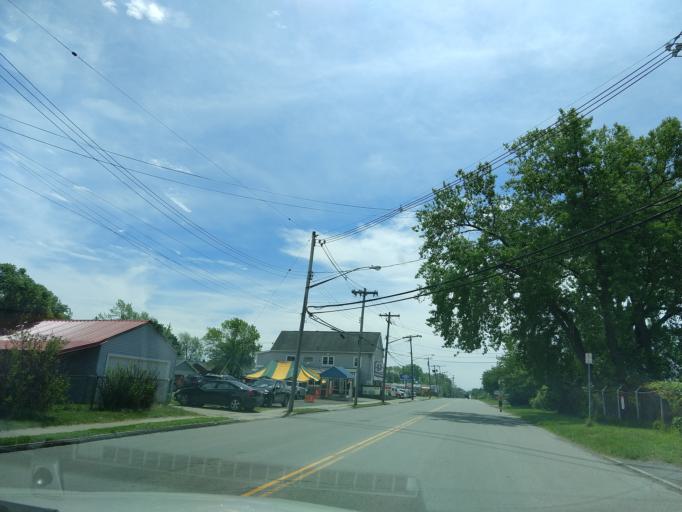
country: US
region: New York
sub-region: Erie County
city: Lackawanna
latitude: 42.8468
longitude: -78.8323
